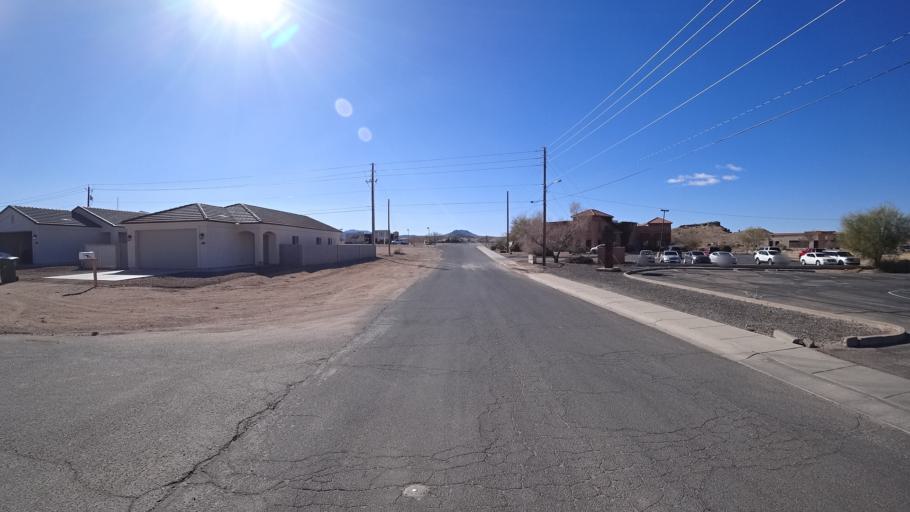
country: US
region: Arizona
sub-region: Mohave County
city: Kingman
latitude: 35.1931
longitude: -114.0247
